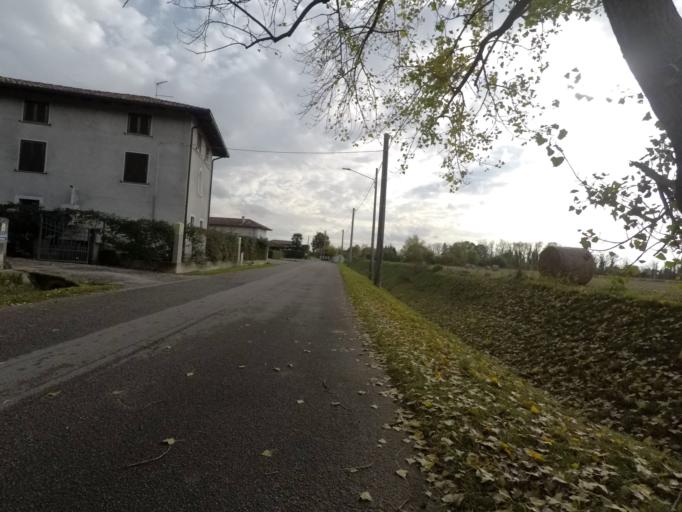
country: IT
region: Friuli Venezia Giulia
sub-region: Provincia di Udine
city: Udine
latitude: 46.0423
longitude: 13.2607
